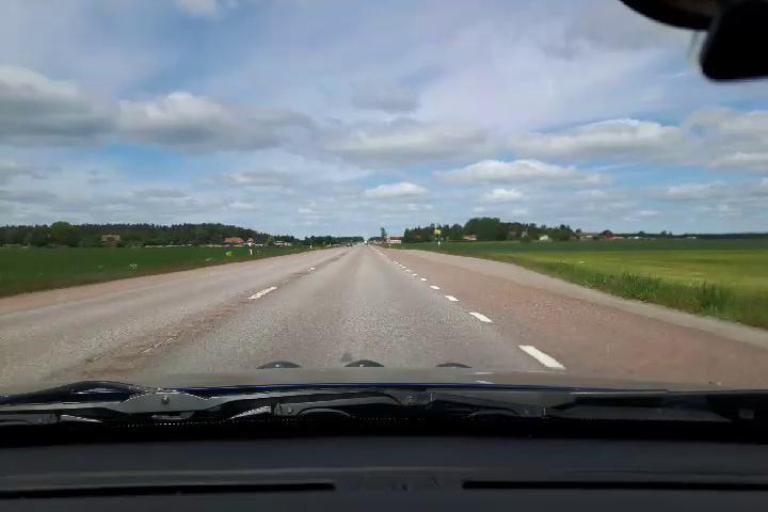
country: SE
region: Uppsala
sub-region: Uppsala Kommun
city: Gamla Uppsala
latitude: 59.9274
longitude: 17.5993
